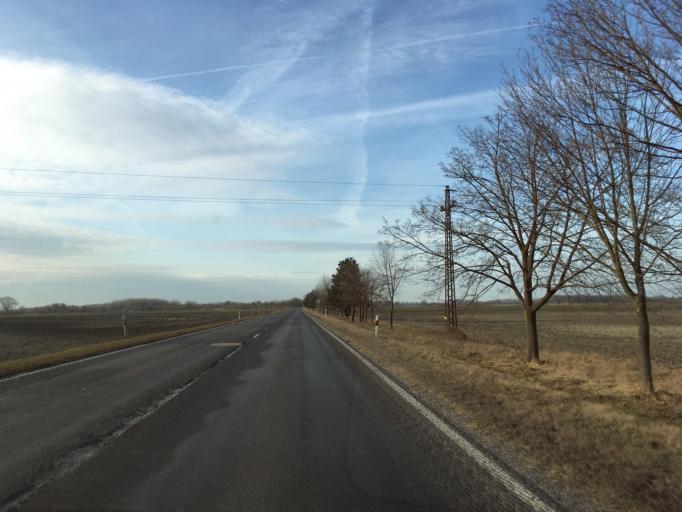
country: HU
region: Gyor-Moson-Sopron
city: Mosonszentmiklos
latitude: 47.7711
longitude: 17.4254
